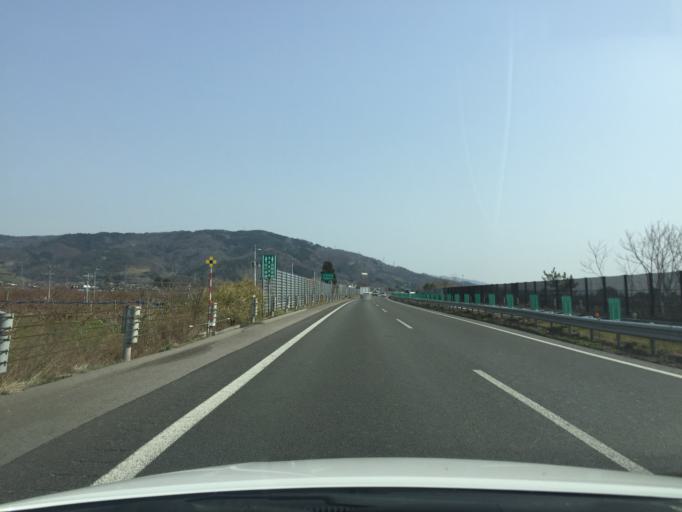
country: JP
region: Fukushima
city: Fukushima-shi
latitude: 37.8171
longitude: 140.4726
